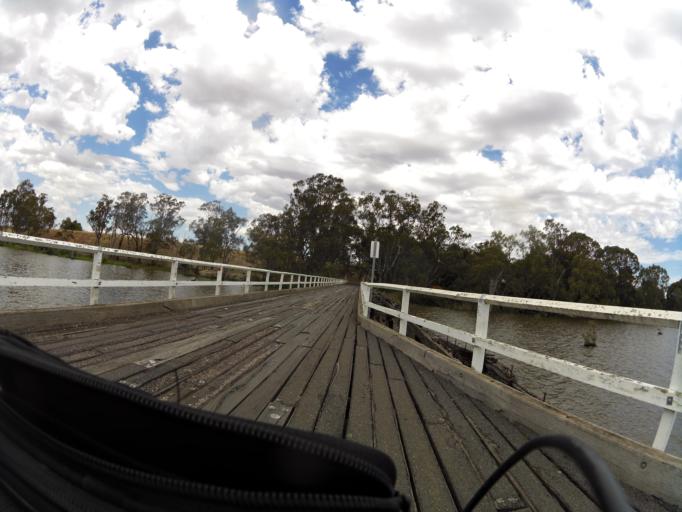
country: AU
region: Victoria
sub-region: Campaspe
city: Kyabram
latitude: -36.7462
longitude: 145.1398
